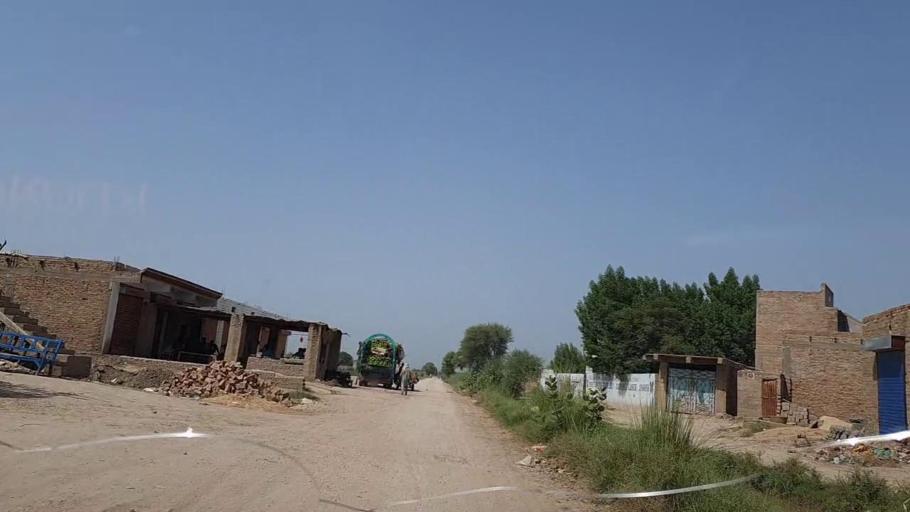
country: PK
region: Sindh
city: Kandiaro
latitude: 27.0305
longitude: 68.1537
